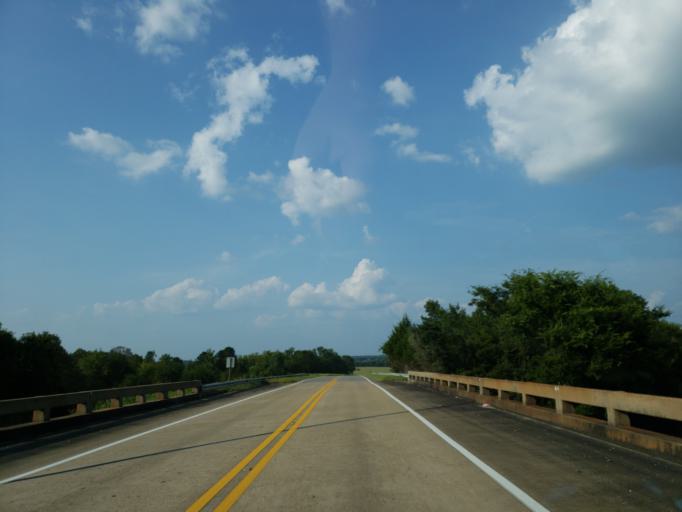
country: US
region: Alabama
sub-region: Greene County
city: Eutaw
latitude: 32.7870
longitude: -87.9757
